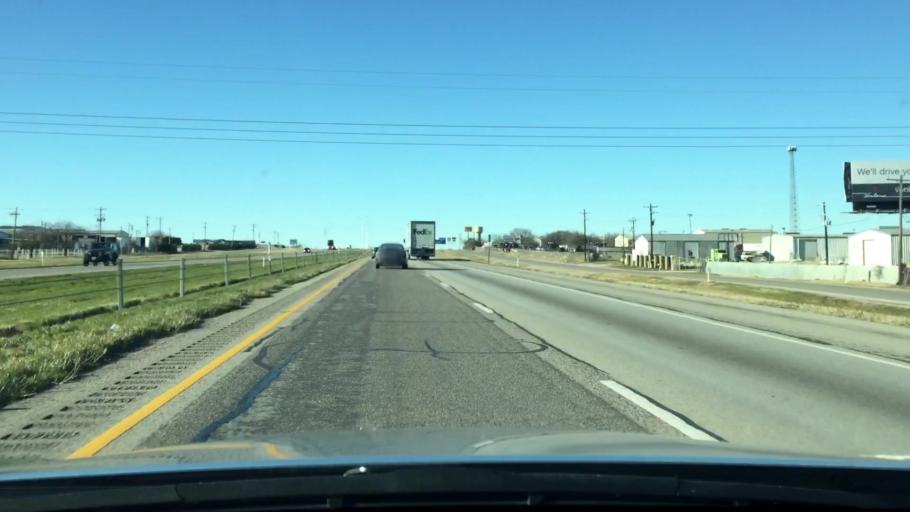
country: US
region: Texas
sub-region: Johnson County
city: Alvarado
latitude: 32.4563
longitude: -97.2607
